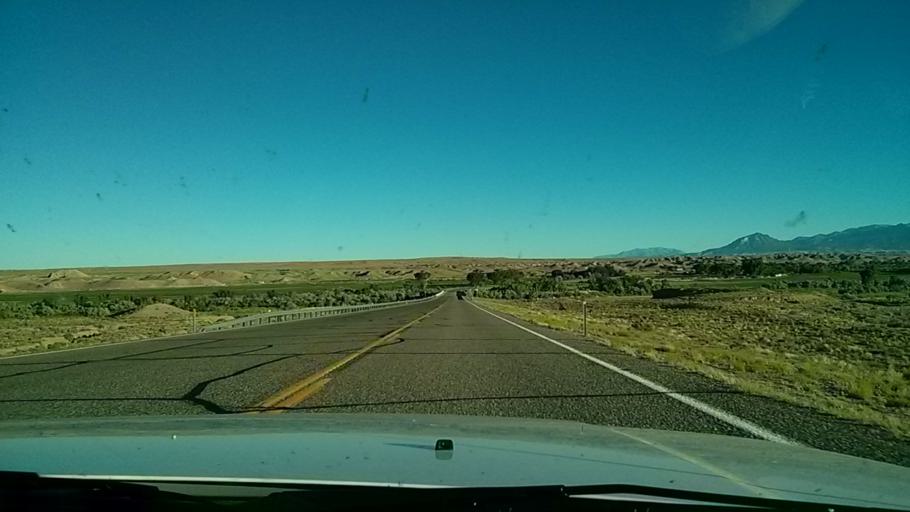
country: US
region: Utah
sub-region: Emery County
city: Ferron
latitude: 38.4074
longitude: -110.6935
